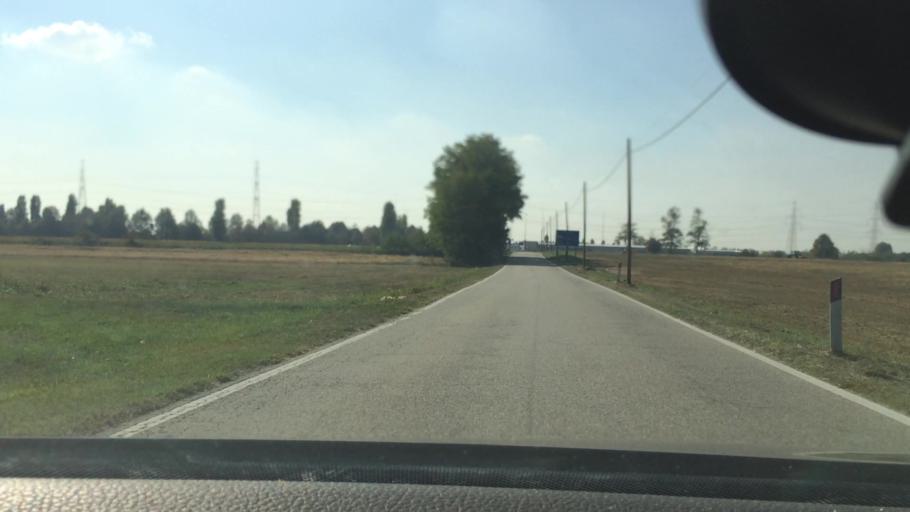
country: IT
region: Lombardy
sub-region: Citta metropolitana di Milano
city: Casate
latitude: 45.4871
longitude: 8.8324
